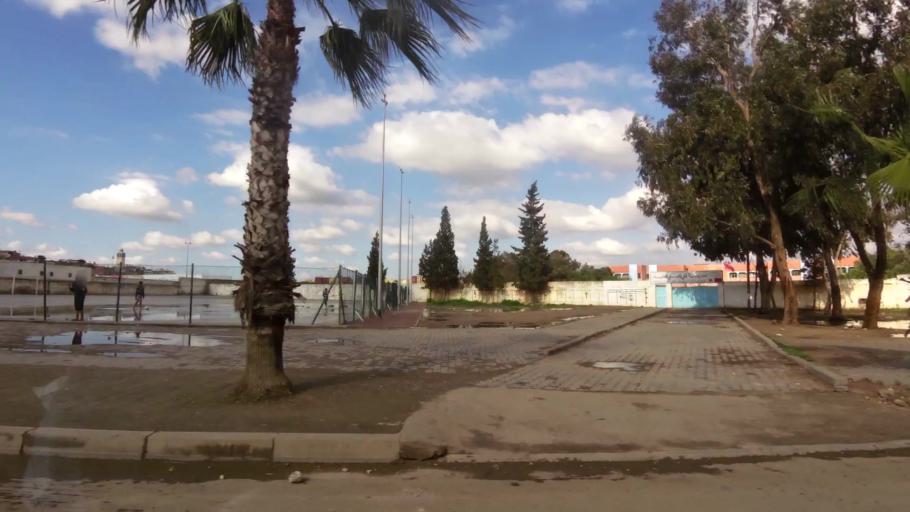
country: MA
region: Chaouia-Ouardigha
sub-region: Settat Province
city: Berrechid
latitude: 33.2698
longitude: -7.5686
